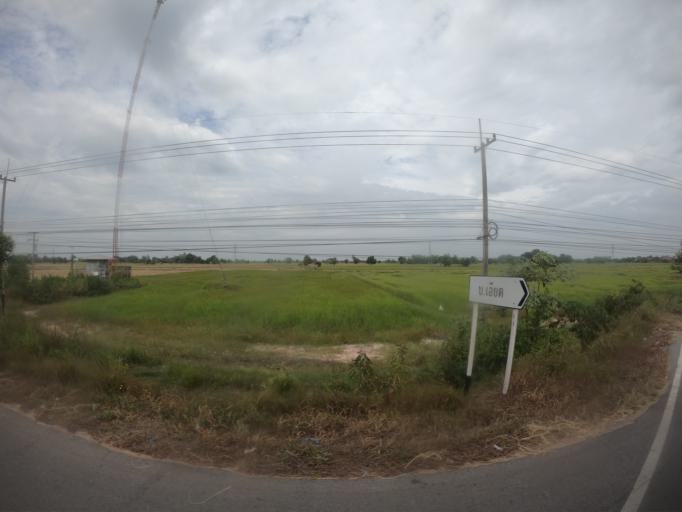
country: TH
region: Maha Sarakham
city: Maha Sarakham
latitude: 16.1504
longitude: 103.3868
